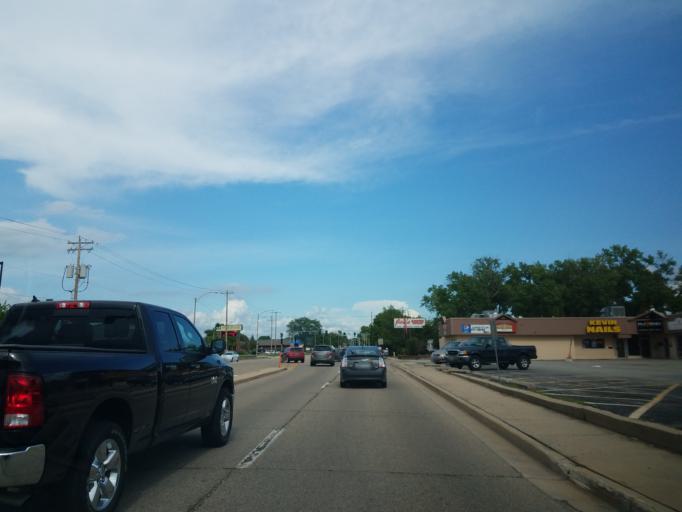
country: US
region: Illinois
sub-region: McLean County
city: Bloomington
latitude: 40.4800
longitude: -88.9523
